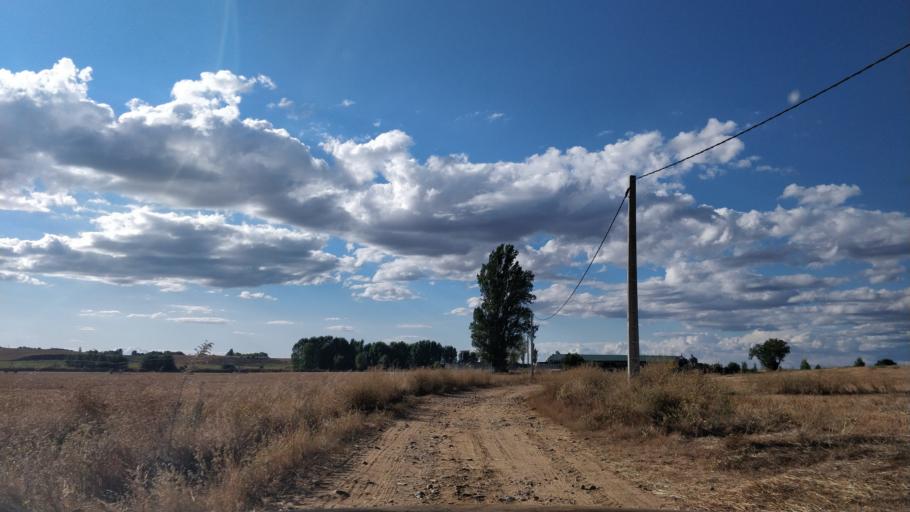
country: ES
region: Castille and Leon
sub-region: Provincia de Leon
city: Valverde-Enrique
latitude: 42.3274
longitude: -5.2789
